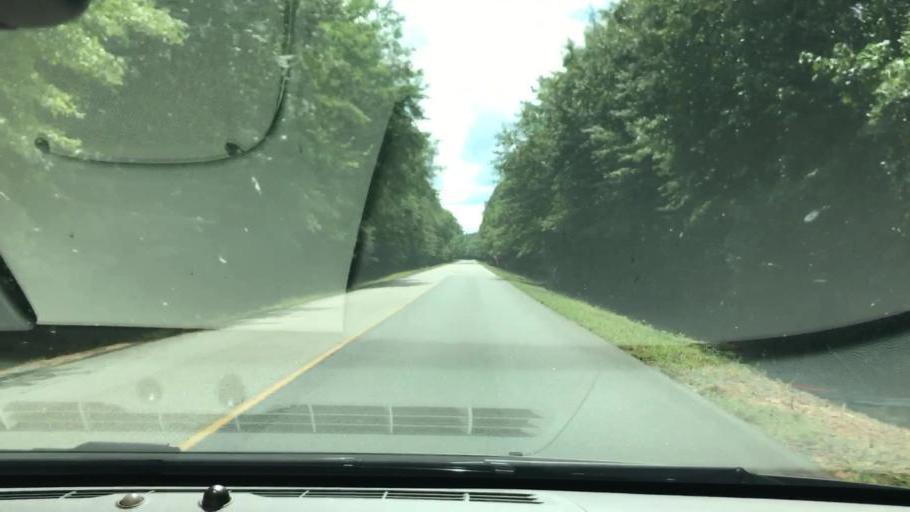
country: US
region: Georgia
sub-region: Quitman County
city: Georgetown
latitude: 31.9910
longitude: -85.0461
